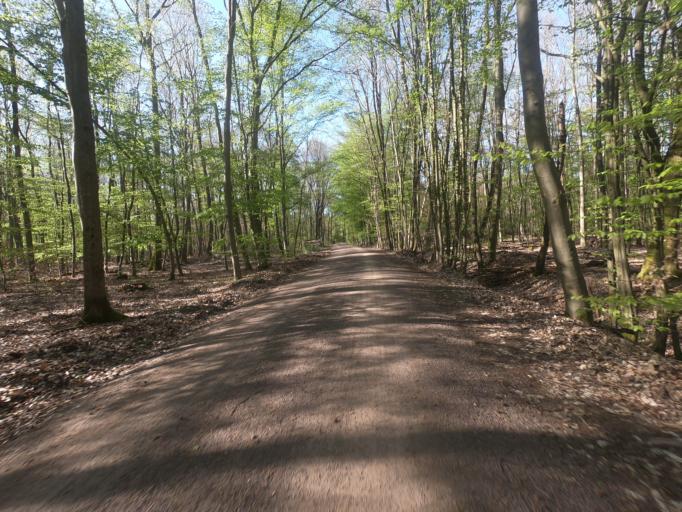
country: DE
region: Hesse
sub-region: Regierungsbezirk Darmstadt
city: Messel
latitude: 49.9632
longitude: 8.7140
